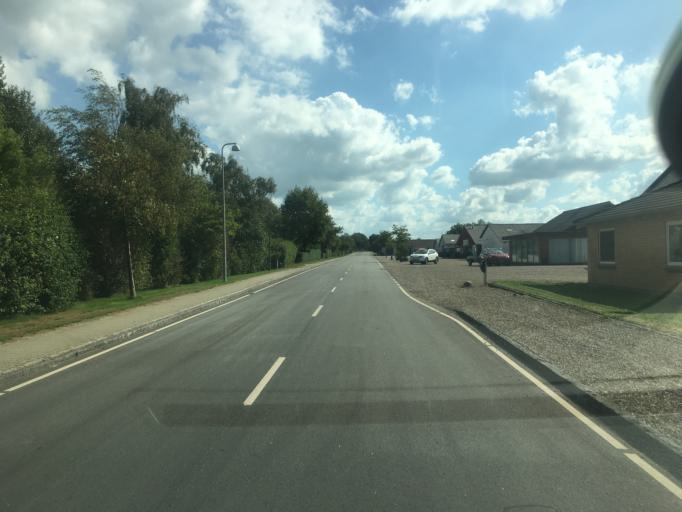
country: DE
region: Schleswig-Holstein
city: Ellhoft
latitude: 54.9379
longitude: 8.9689
